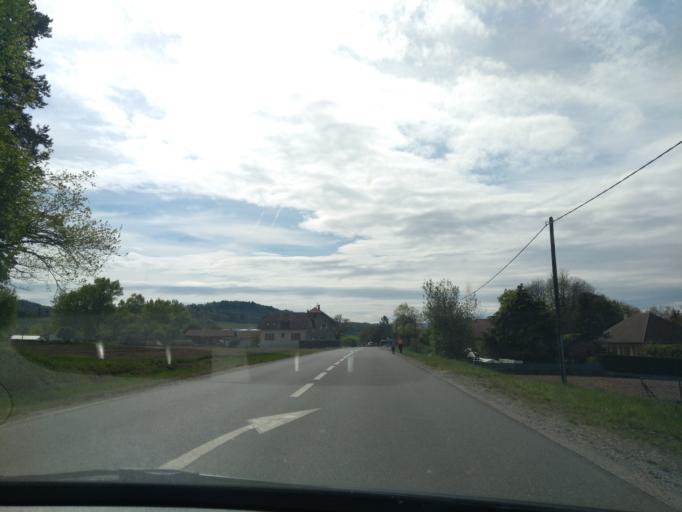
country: FR
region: Rhone-Alpes
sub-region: Departement de la Haute-Savoie
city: Chavanod
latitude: 45.8806
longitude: 6.0460
